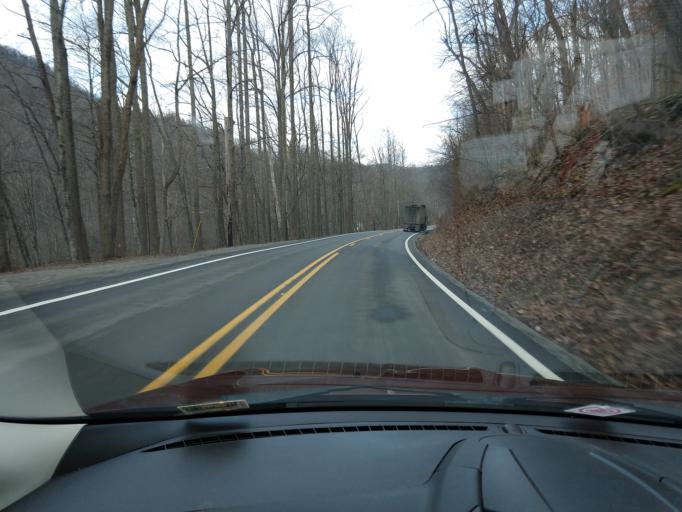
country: US
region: West Virginia
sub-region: Randolph County
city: Elkins
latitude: 38.6606
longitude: -79.9364
